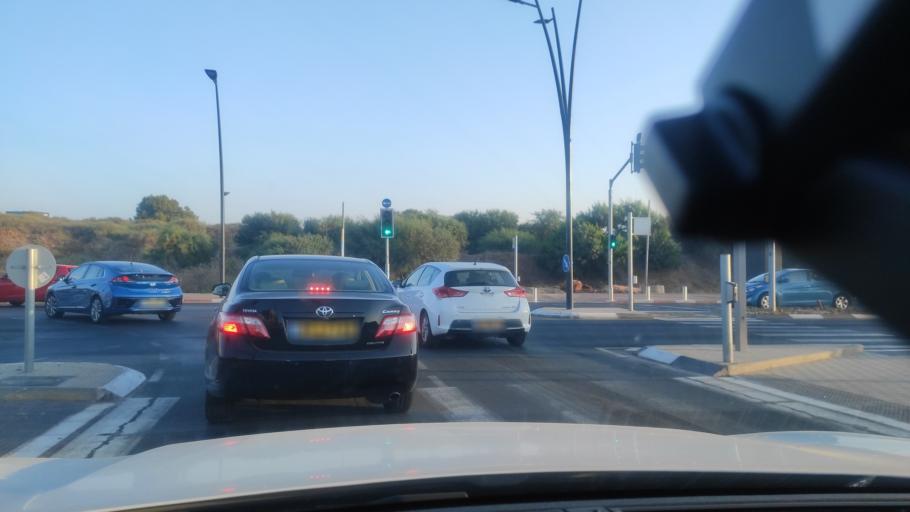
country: IL
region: Tel Aviv
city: Herzliya Pituah
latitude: 32.1641
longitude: 34.8026
